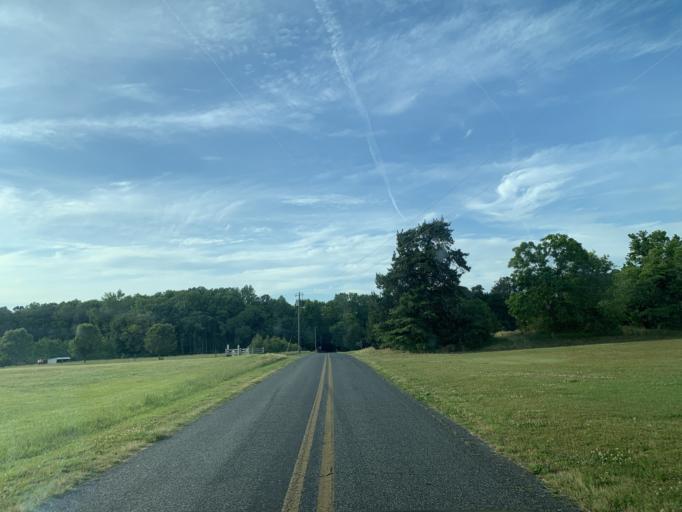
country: US
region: Maryland
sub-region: Worcester County
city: Pocomoke City
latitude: 38.0899
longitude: -75.4641
